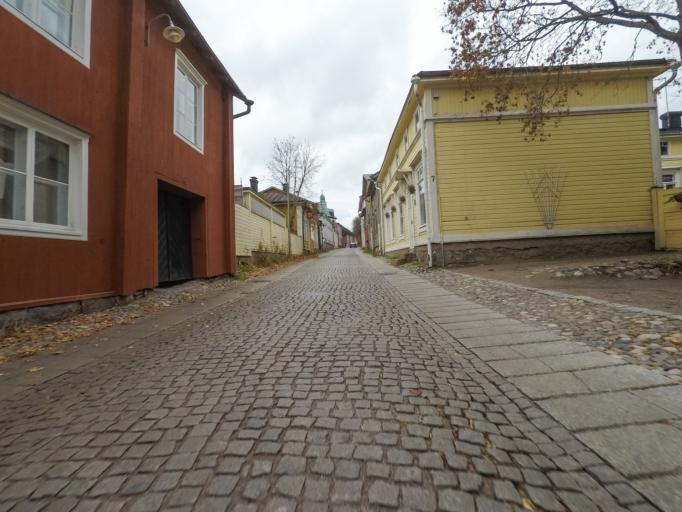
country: FI
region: Uusimaa
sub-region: Porvoo
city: Porvoo
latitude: 60.3959
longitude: 25.6602
